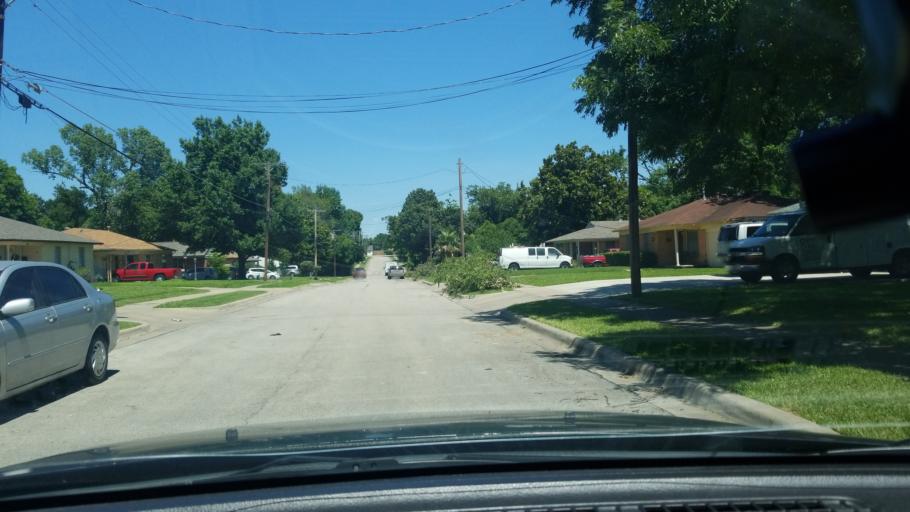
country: US
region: Texas
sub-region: Dallas County
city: Mesquite
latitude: 32.7607
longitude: -96.6090
